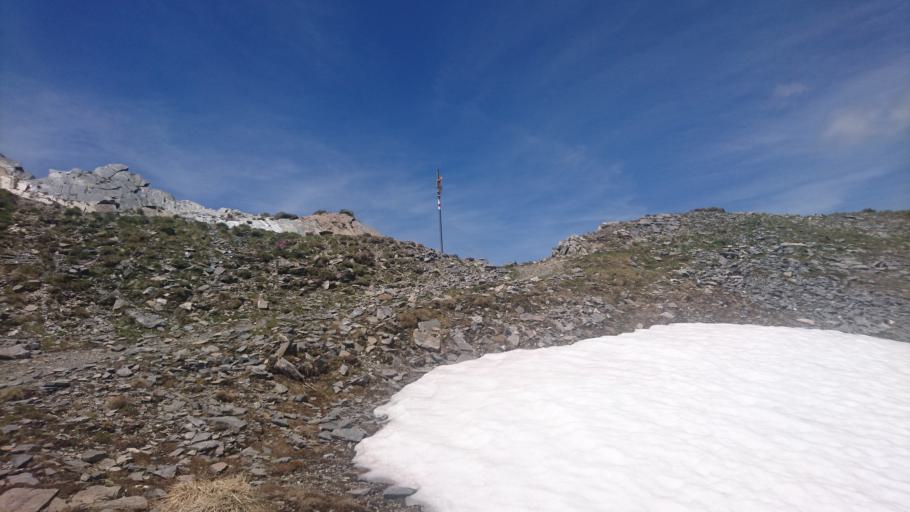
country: CH
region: Grisons
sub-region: Hinterrhein District
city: Thusis
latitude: 46.6354
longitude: 9.3453
